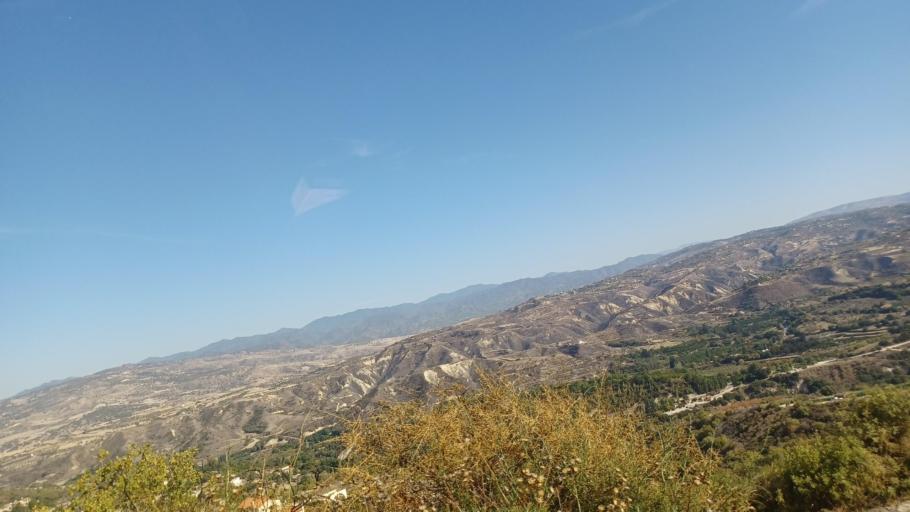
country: CY
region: Pafos
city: Pegeia
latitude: 34.9334
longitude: 32.4545
